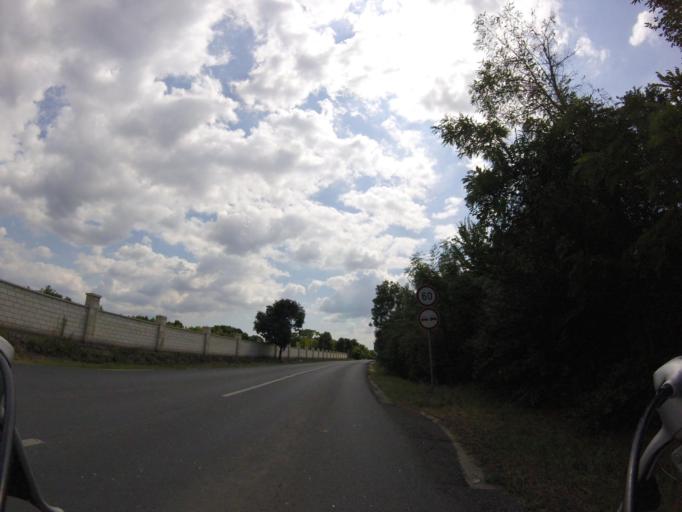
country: HU
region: Pest
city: Soskut
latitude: 47.4331
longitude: 18.8236
